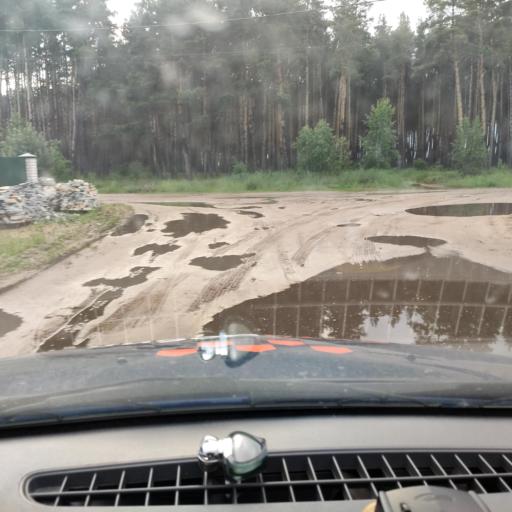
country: RU
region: Voronezj
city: Somovo
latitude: 51.7548
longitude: 39.3222
